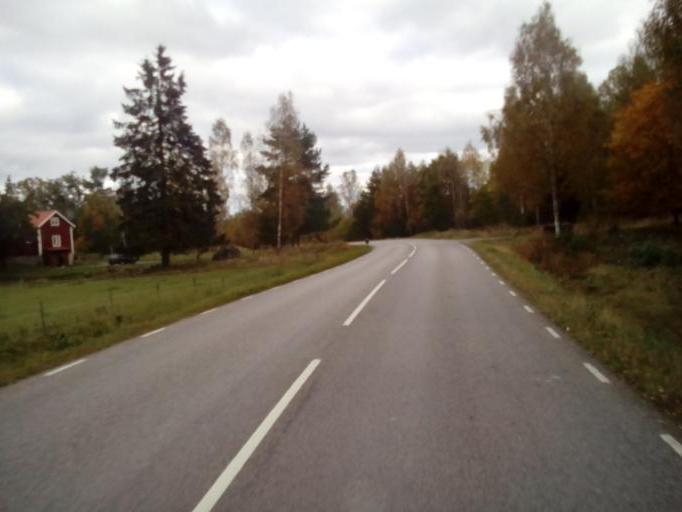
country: SE
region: Kalmar
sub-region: Vasterviks Kommun
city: Gamleby
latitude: 57.8761
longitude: 16.3133
